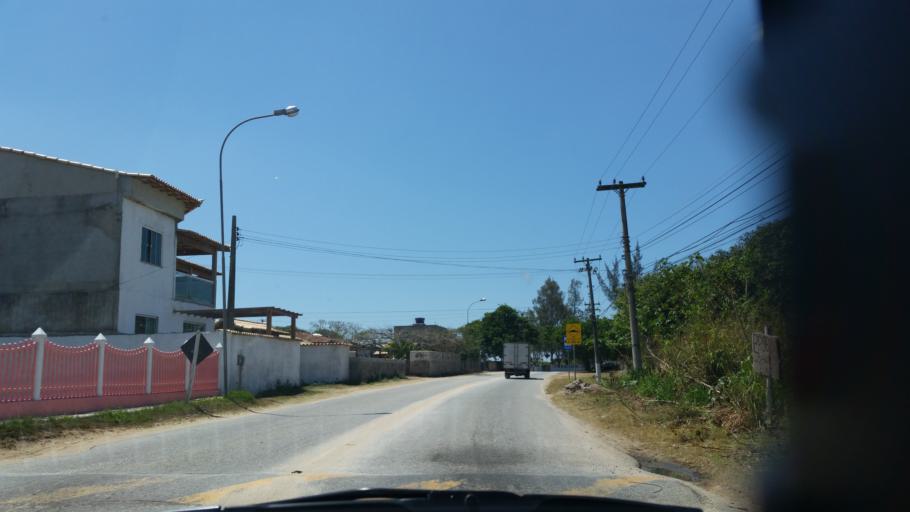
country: BR
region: Rio de Janeiro
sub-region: Cabo Frio
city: Cabo Frio
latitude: -22.8317
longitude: -41.9911
